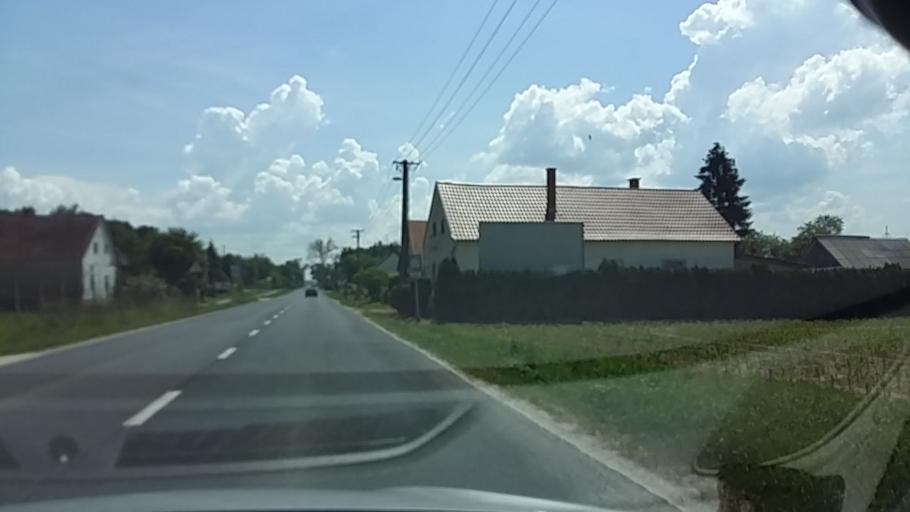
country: AT
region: Burgenland
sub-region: Politischer Bezirk Gussing
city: Inzenhof
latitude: 46.9764
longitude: 16.3708
